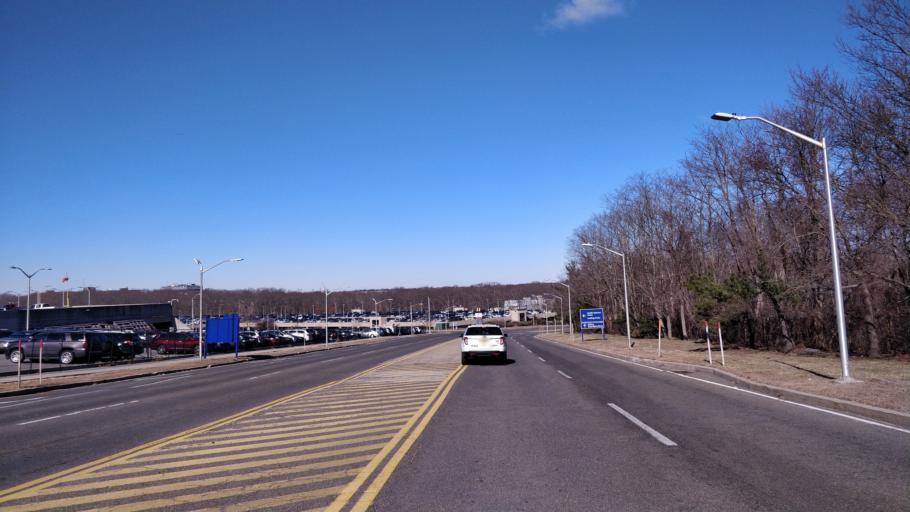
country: US
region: New York
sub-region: Suffolk County
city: Setauket-East Setauket
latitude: 40.9091
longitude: -73.1123
